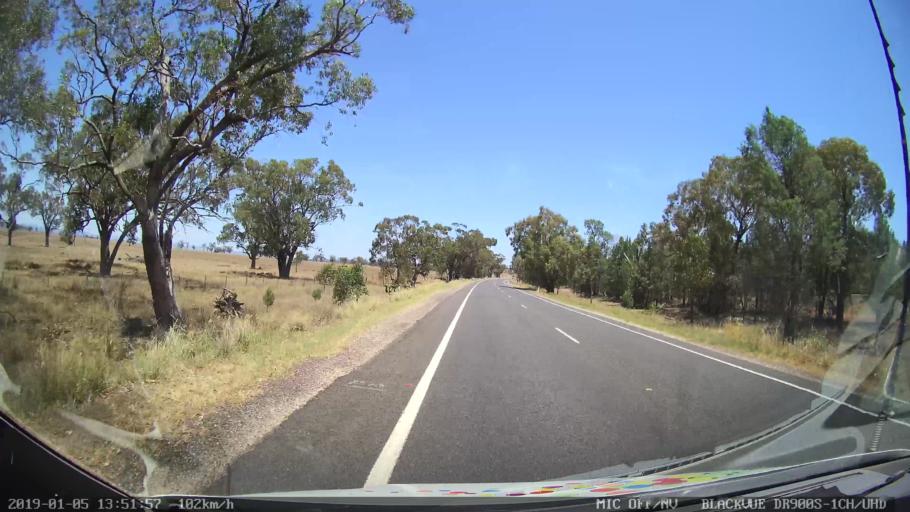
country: AU
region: New South Wales
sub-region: Gunnedah
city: Gunnedah
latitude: -31.0523
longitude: 150.2778
